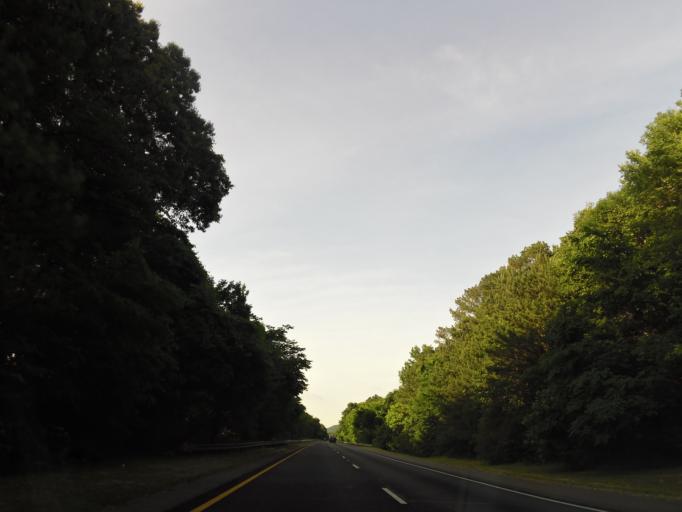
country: US
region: Alabama
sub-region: DeKalb County
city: Collinsville
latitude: 34.2059
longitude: -85.9390
